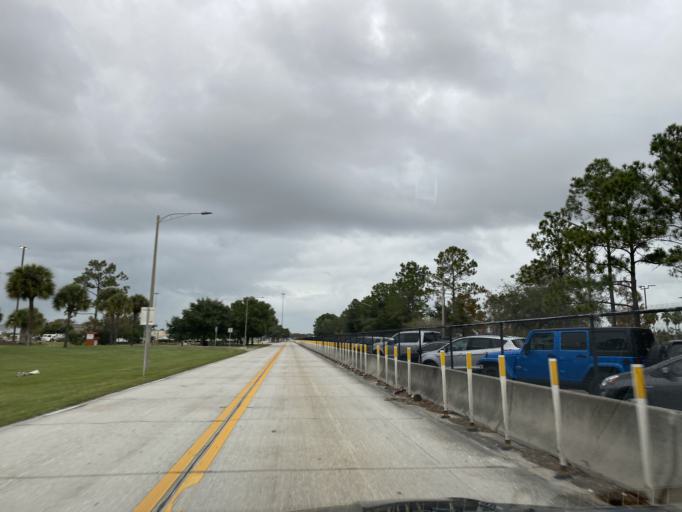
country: US
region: Florida
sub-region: Orange County
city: Belle Isle
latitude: 28.4437
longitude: -81.3154
